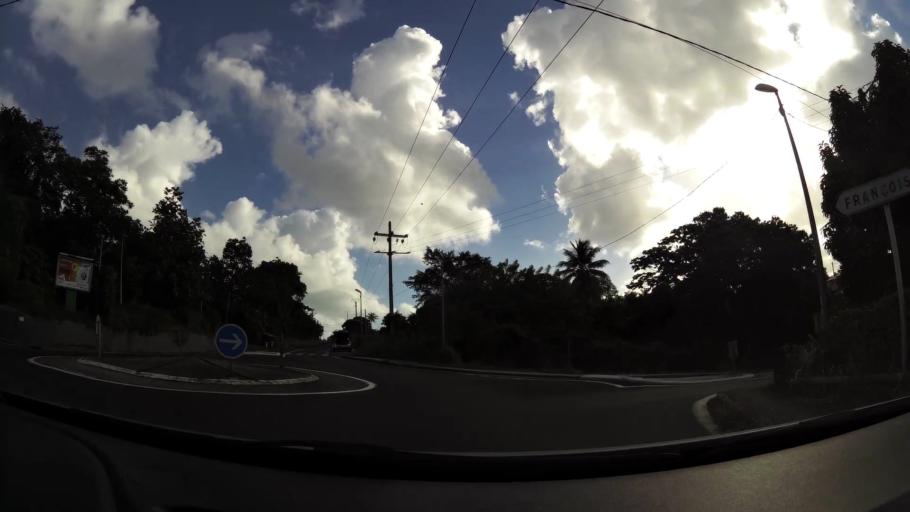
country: MQ
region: Martinique
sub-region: Martinique
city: Ducos
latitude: 14.5995
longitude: -60.9436
